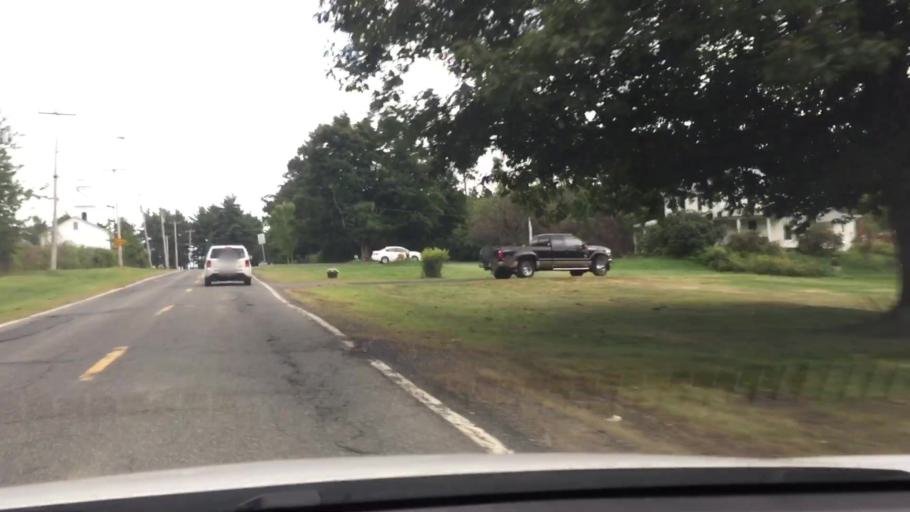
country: US
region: Massachusetts
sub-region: Hampden County
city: Granville
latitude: 42.1839
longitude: -72.9302
